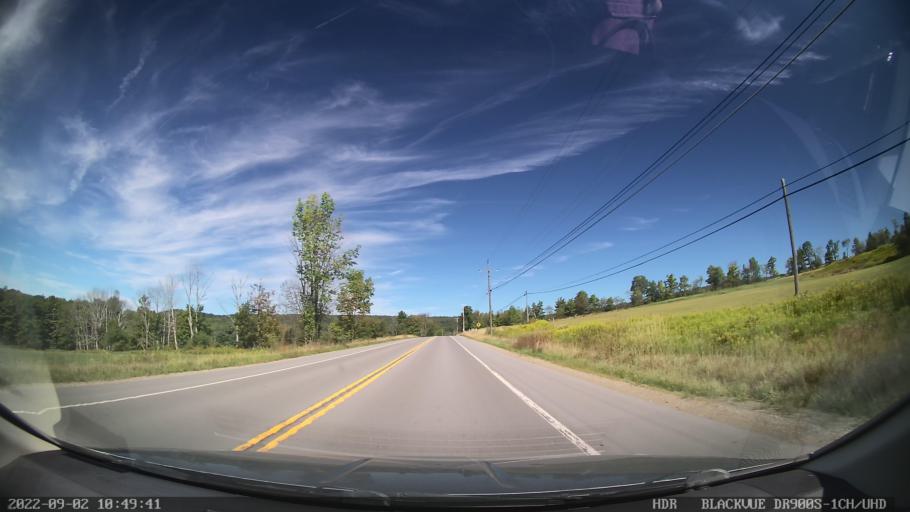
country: US
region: Pennsylvania
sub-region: Tioga County
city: Blossburg
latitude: 41.6036
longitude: -77.1133
